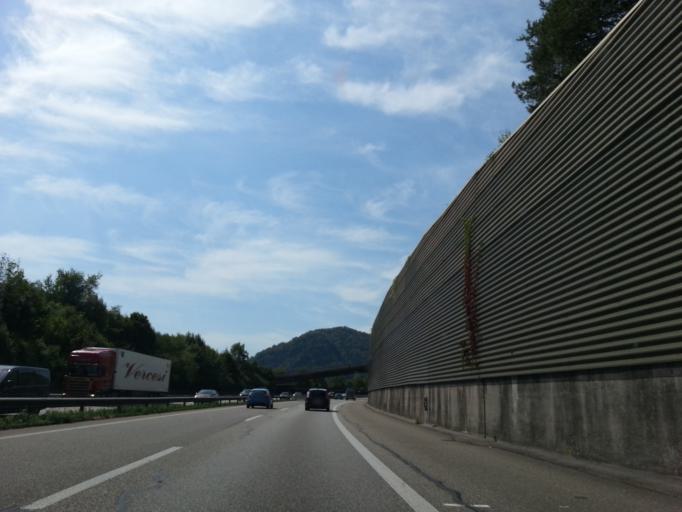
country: CH
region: Basel-Landschaft
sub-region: Bezirk Waldenburg
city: Diegten
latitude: 47.4137
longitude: 7.8091
